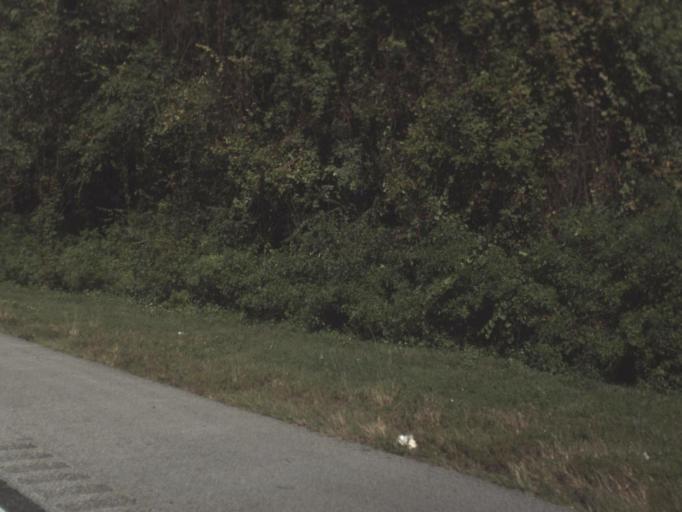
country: US
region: Florida
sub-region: Sumter County
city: Wildwood
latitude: 28.8501
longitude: -82.0830
